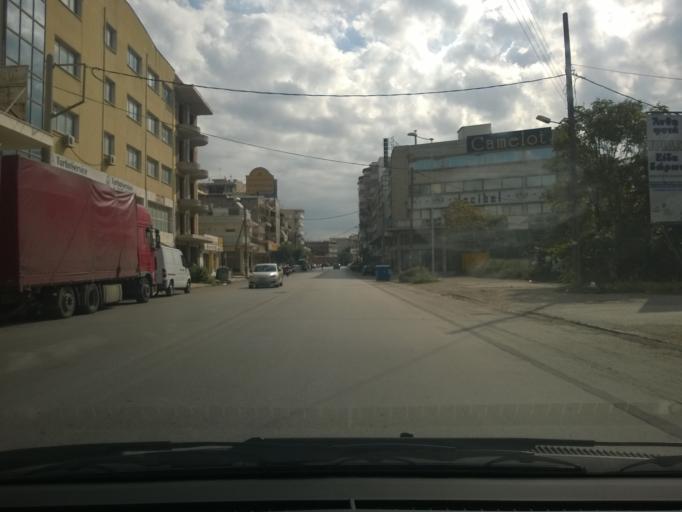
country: GR
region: Central Macedonia
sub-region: Nomos Thessalonikis
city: Ampelokipoi
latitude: 40.6512
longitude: 22.9130
